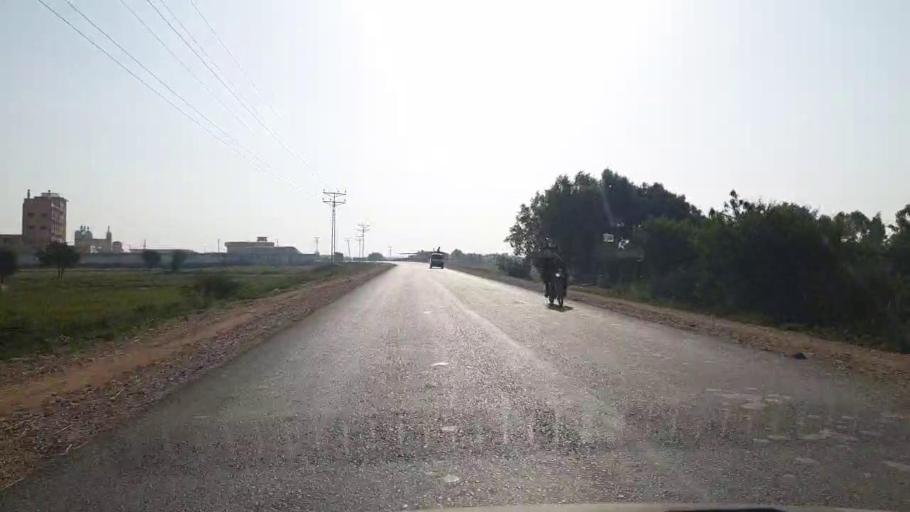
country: PK
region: Sindh
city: Badin
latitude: 24.6614
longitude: 68.8777
